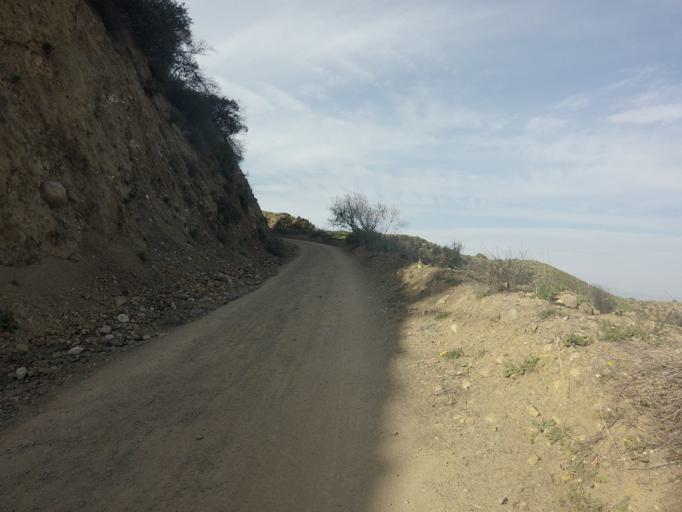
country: US
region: California
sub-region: Riverside County
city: Corona
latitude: 33.8377
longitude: -117.6124
